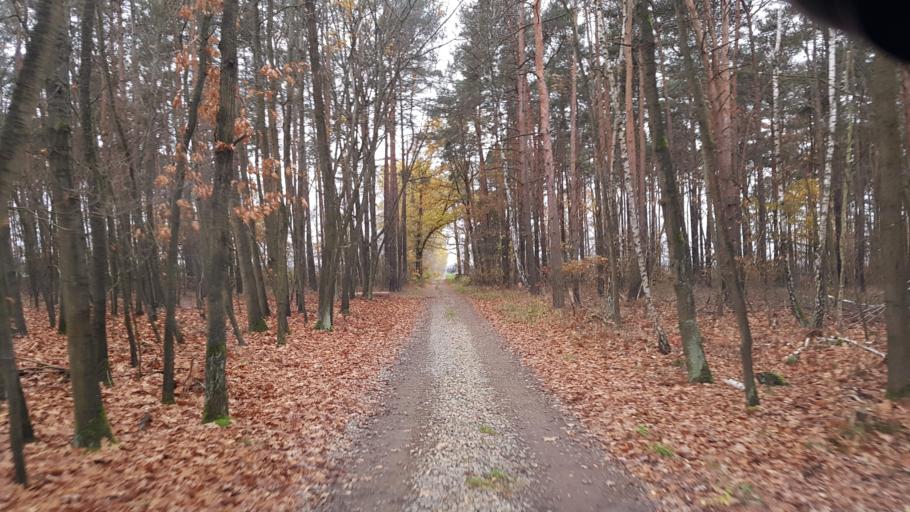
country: DE
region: Brandenburg
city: Sallgast
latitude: 51.6171
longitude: 13.8785
